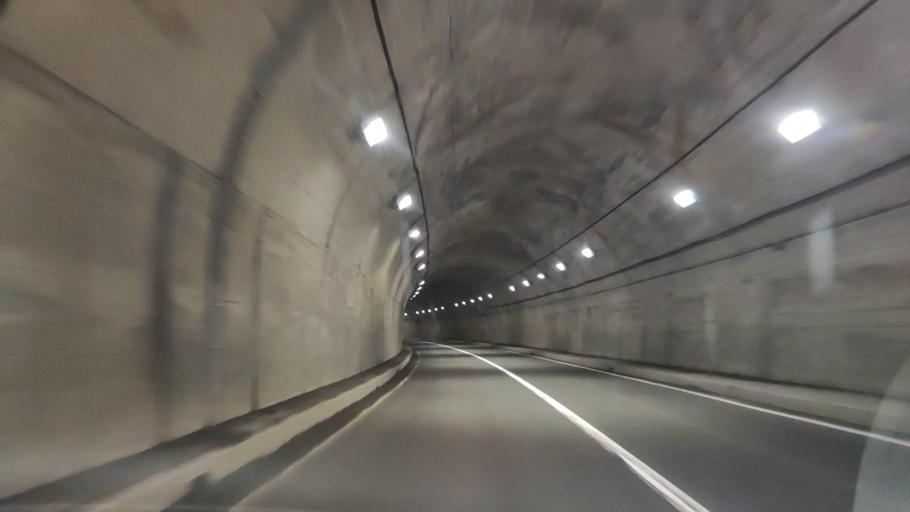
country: JP
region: Akita
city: Yuzawa
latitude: 39.0536
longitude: 140.4400
